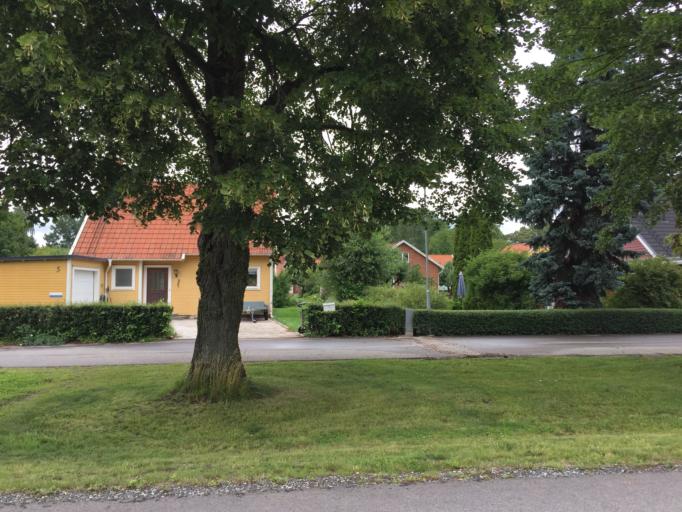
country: SE
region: Soedermanland
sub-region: Vingakers Kommun
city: Vingaker
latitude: 59.0427
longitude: 15.8802
